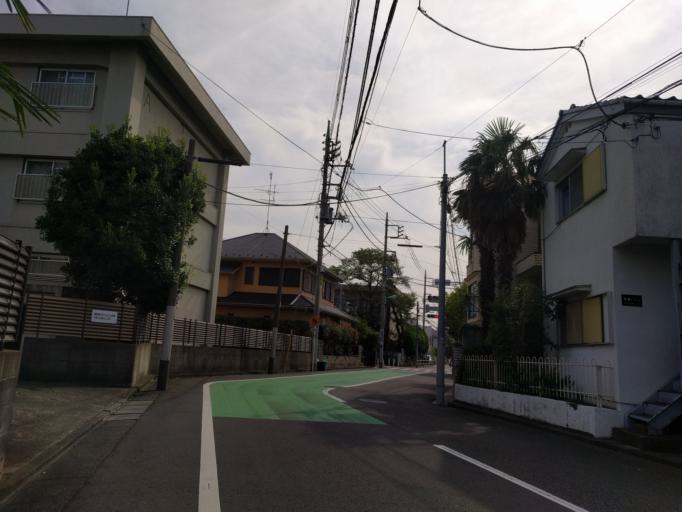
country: JP
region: Tokyo
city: Tokyo
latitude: 35.6488
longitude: 139.6495
